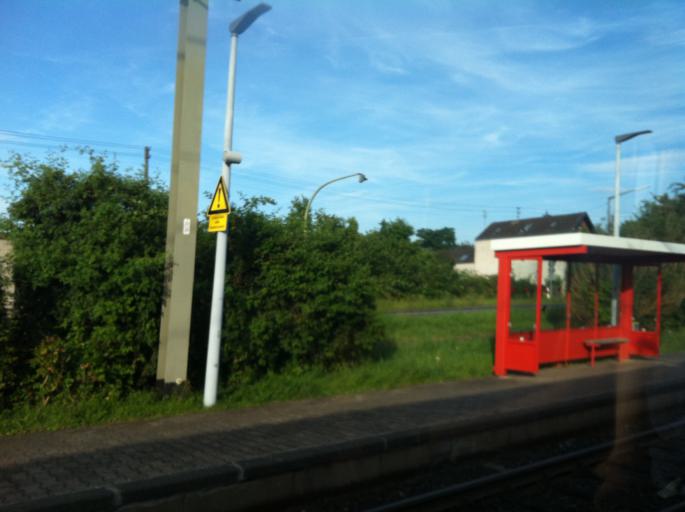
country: DE
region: North Rhine-Westphalia
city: Niederkassel
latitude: 50.7822
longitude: 7.0312
